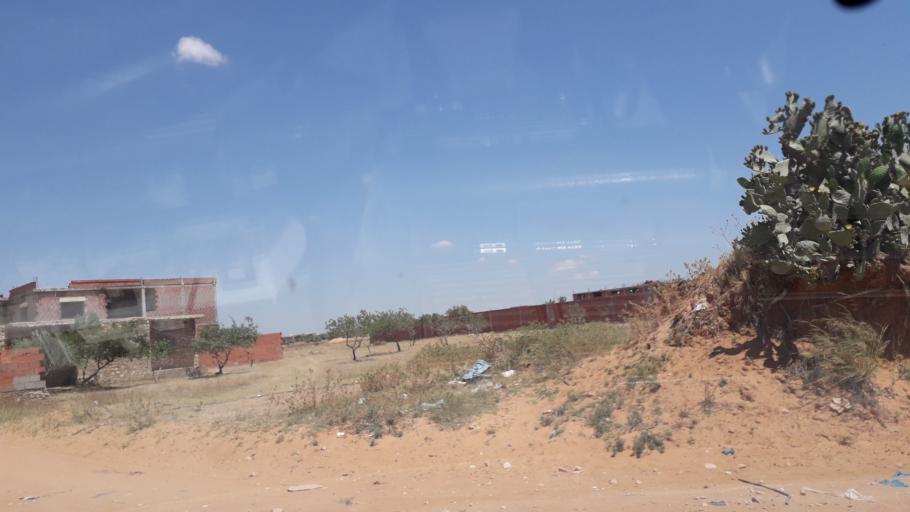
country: TN
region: Safaqis
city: Al Qarmadah
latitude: 34.8311
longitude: 10.7770
